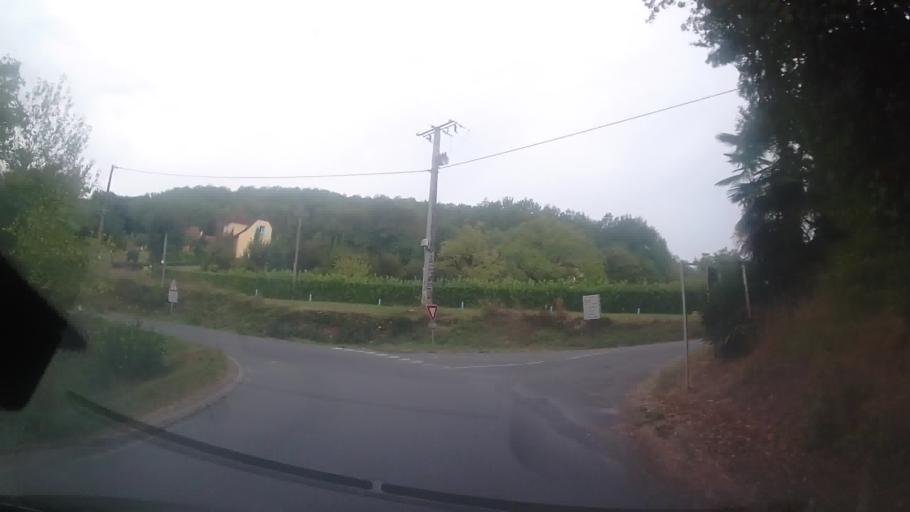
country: FR
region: Aquitaine
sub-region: Departement de la Dordogne
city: Carsac-Aillac
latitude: 44.8454
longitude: 1.2544
